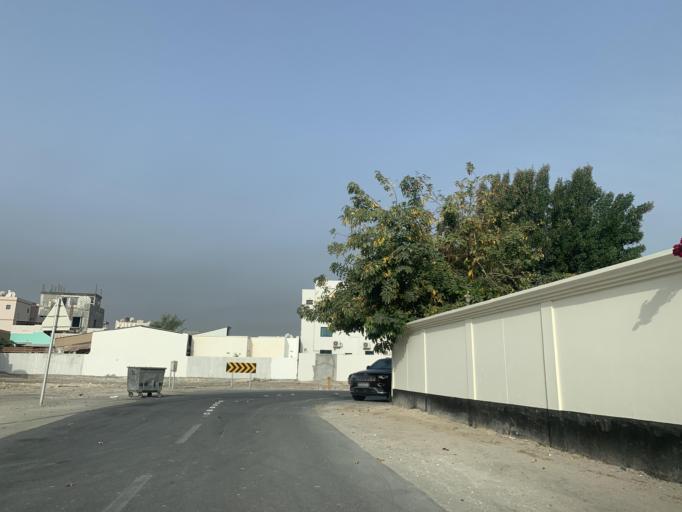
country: BH
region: Northern
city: Madinat `Isa
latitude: 26.1905
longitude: 50.5621
